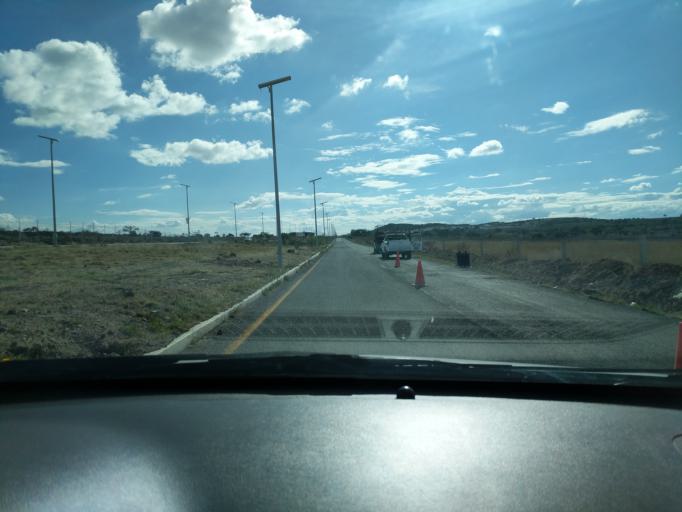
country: MX
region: Queretaro
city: La Canada
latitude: 20.5969
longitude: -100.2951
